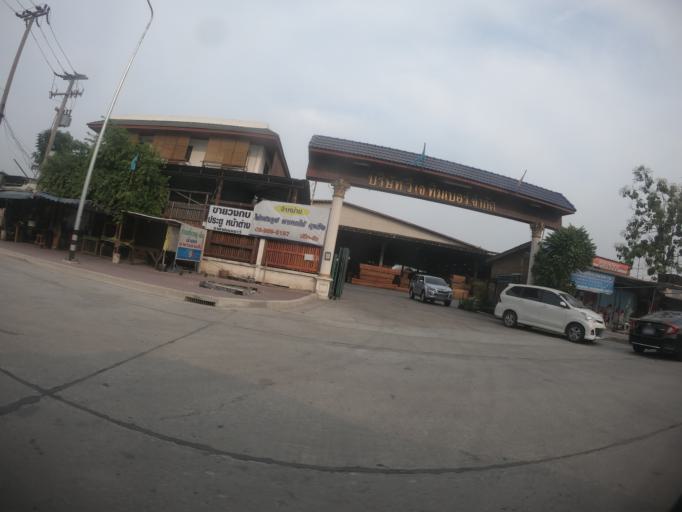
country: TH
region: Phra Nakhon Si Ayutthaya
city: Ban Bang Kadi Pathum Thani
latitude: 14.0014
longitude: 100.5706
